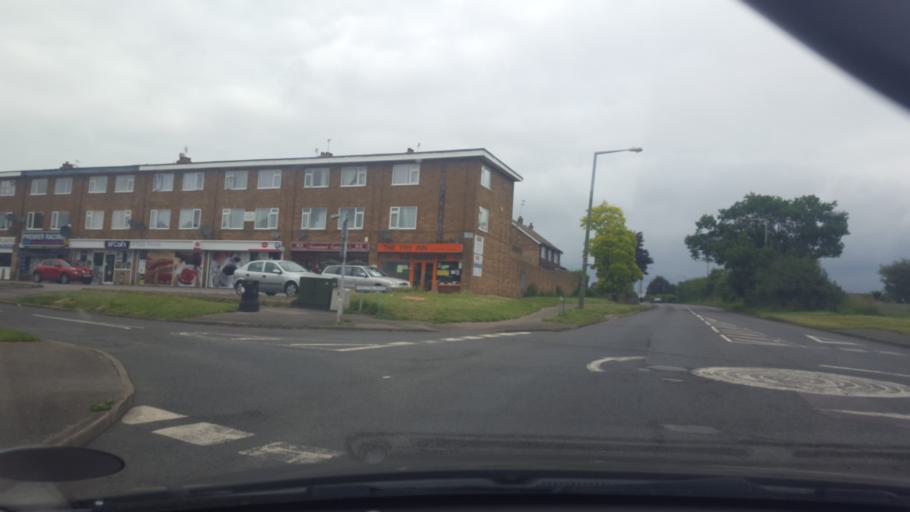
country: GB
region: England
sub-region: Essex
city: Clacton-on-Sea
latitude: 51.7825
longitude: 1.1202
